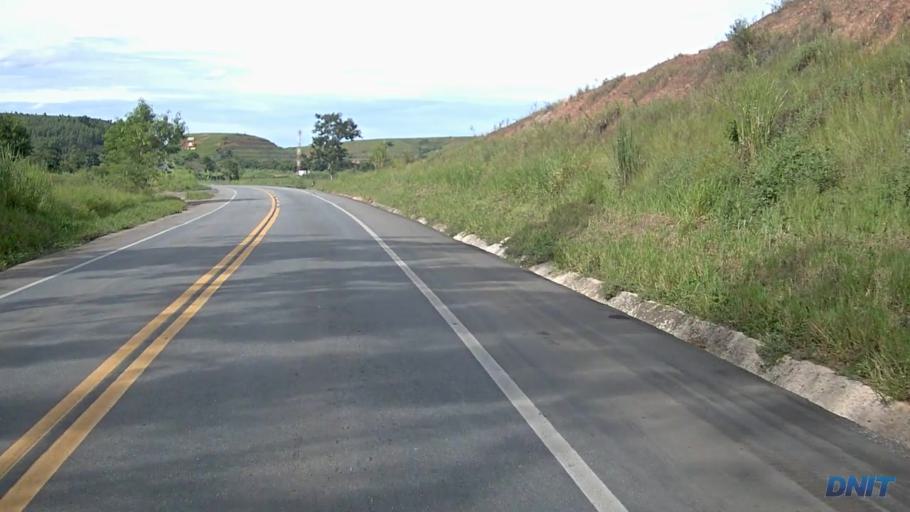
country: BR
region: Minas Gerais
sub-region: Belo Oriente
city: Belo Oriente
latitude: -19.2607
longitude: -42.3435
